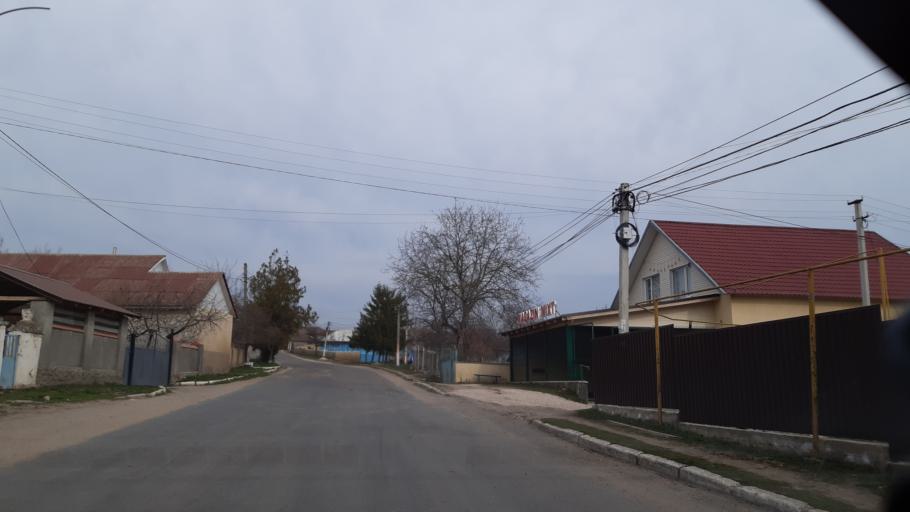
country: MD
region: Soldanesti
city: Soldanesti
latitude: 47.6841
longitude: 28.7641
